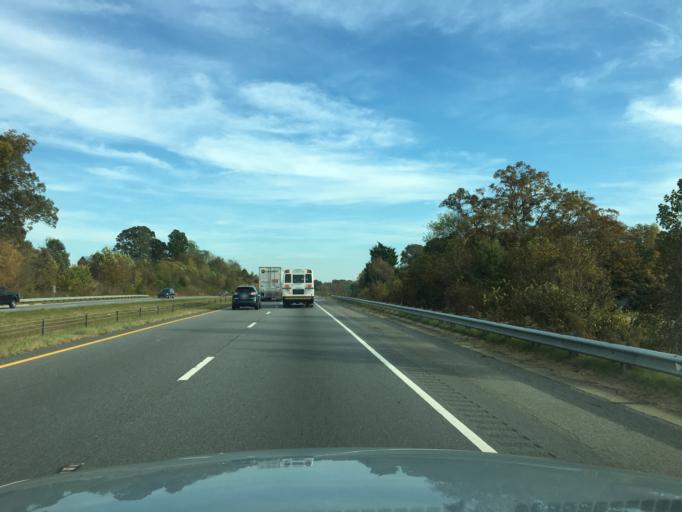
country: US
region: North Carolina
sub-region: Catawba County
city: Maiden
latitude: 35.6157
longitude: -81.2819
